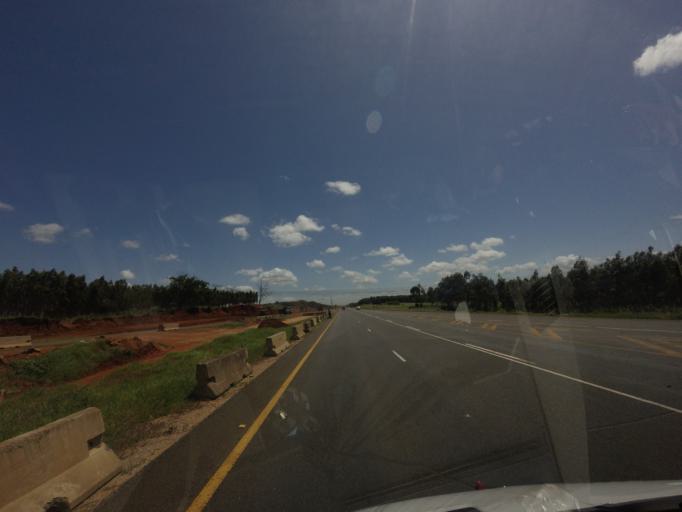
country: ZA
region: KwaZulu-Natal
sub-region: uThungulu District Municipality
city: Empangeni
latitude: -28.7651
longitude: 31.9319
